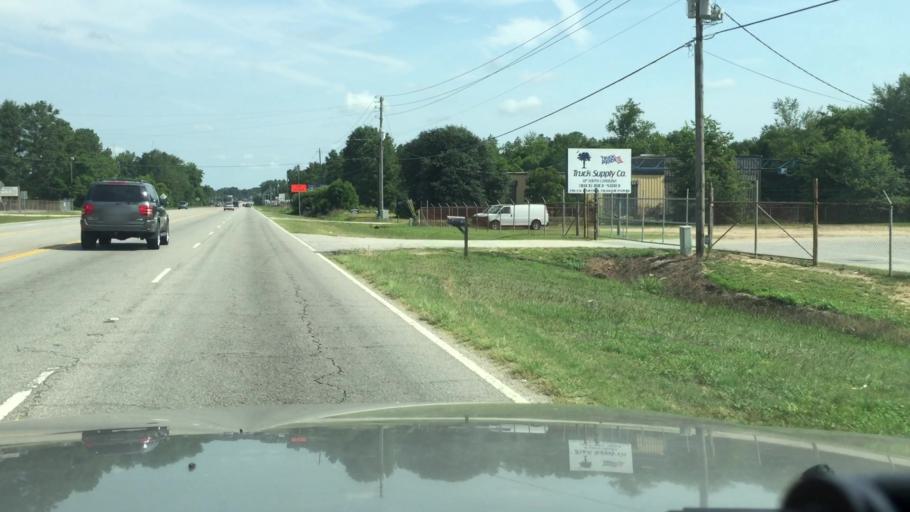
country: US
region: South Carolina
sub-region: Sumter County
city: South Sumter
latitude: 33.8894
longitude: -80.3509
